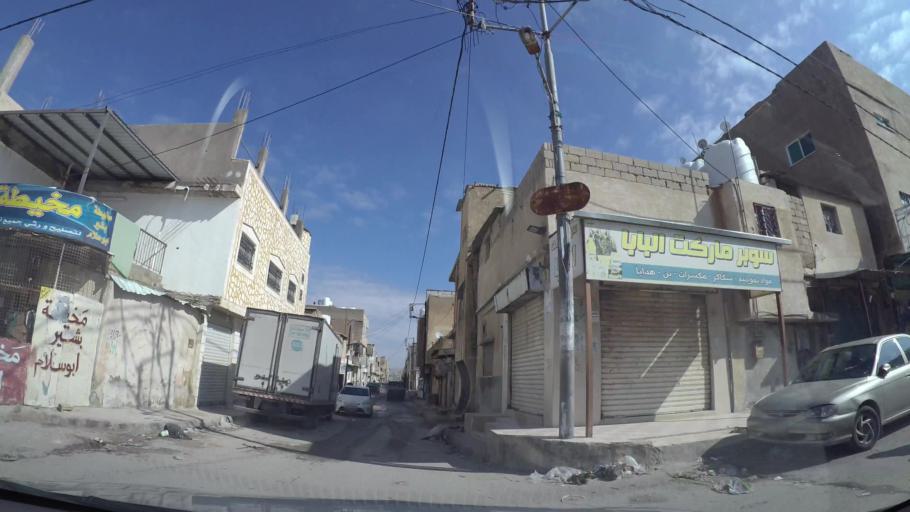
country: JO
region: Amman
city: Al Jubayhah
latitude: 32.0737
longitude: 35.8467
